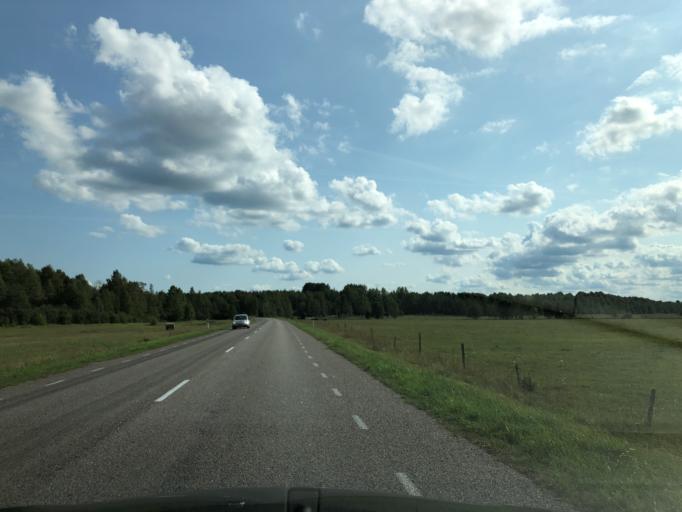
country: EE
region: Hiiumaa
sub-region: Kaerdla linn
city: Kardla
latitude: 58.7225
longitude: 22.5625
